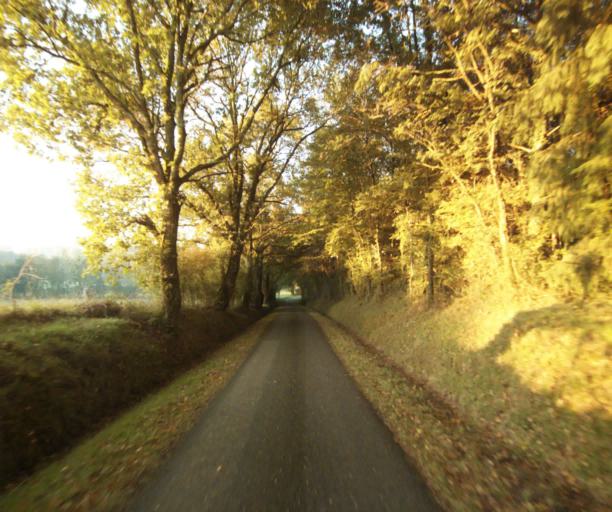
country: FR
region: Midi-Pyrenees
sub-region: Departement du Gers
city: Gondrin
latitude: 43.7944
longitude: 0.1842
